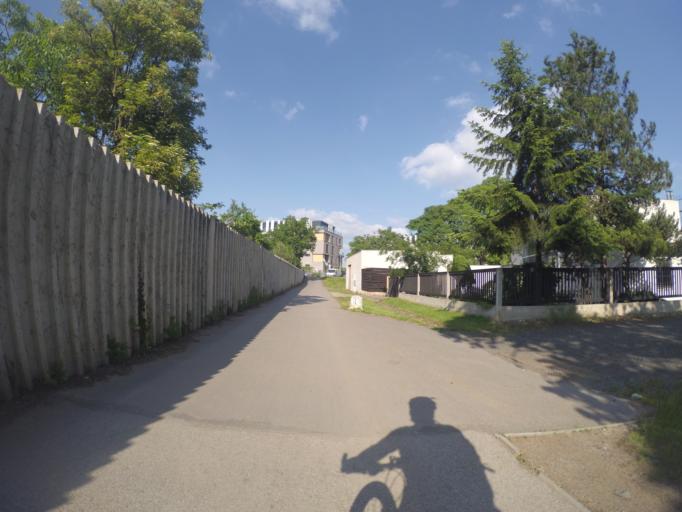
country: CZ
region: Praha
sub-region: Praha 8
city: Liben
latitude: 50.1055
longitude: 14.4643
